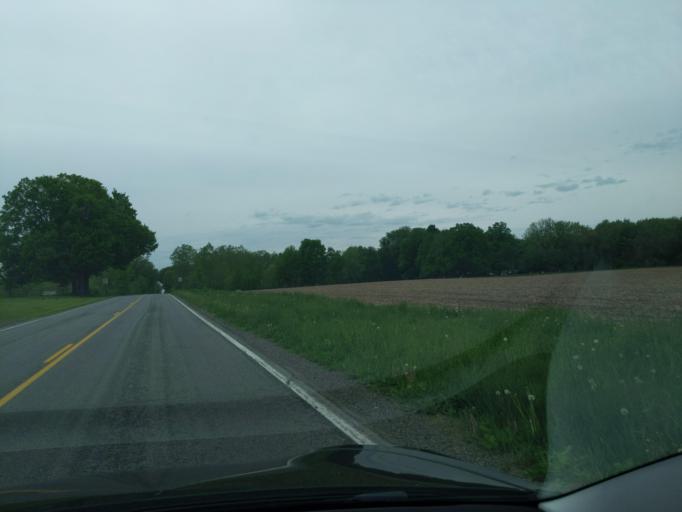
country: US
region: Michigan
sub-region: Ingham County
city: Leslie
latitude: 42.4475
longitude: -84.3722
